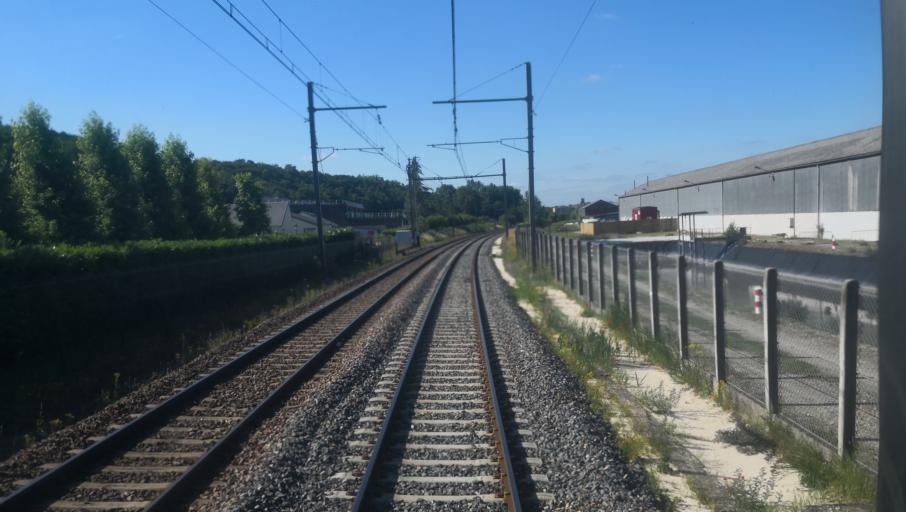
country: FR
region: Ile-de-France
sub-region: Departement de Seine-et-Marne
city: Bagneaux-sur-Loing
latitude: 48.2309
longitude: 2.7032
